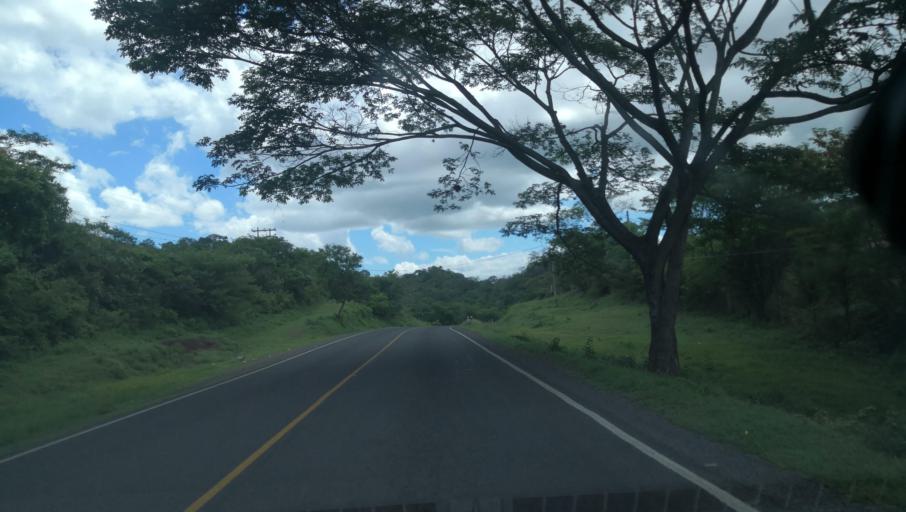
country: NI
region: Madriz
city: Palacaguina
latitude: 13.4440
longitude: -86.4396
